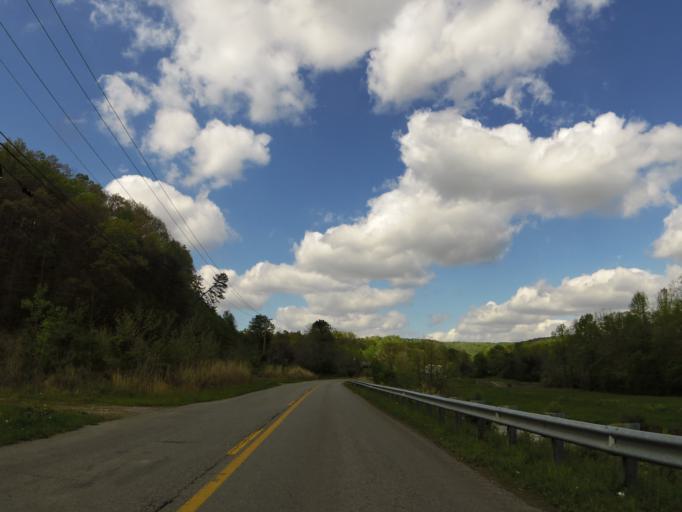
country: US
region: Kentucky
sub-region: Bell County
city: Middlesboro
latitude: 36.6263
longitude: -83.7353
